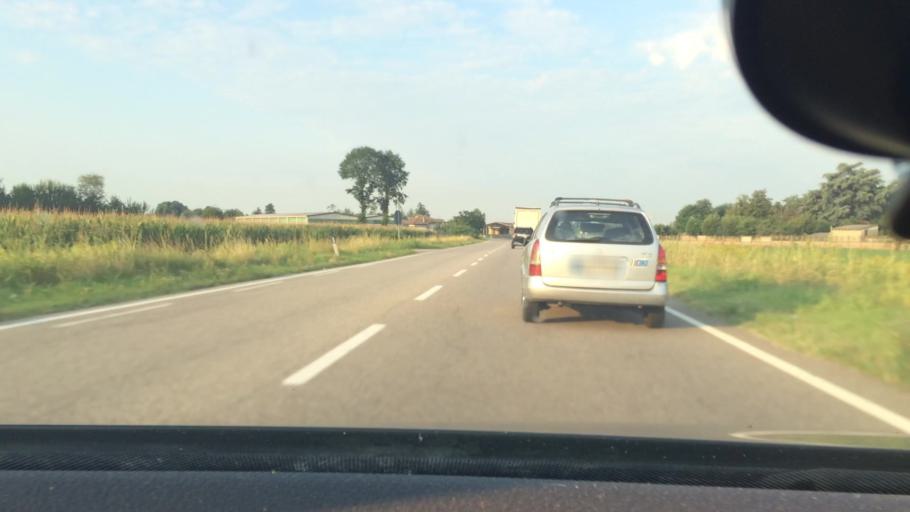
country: IT
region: Lombardy
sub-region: Citta metropolitana di Milano
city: Casorezzo
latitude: 45.5149
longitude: 8.9098
